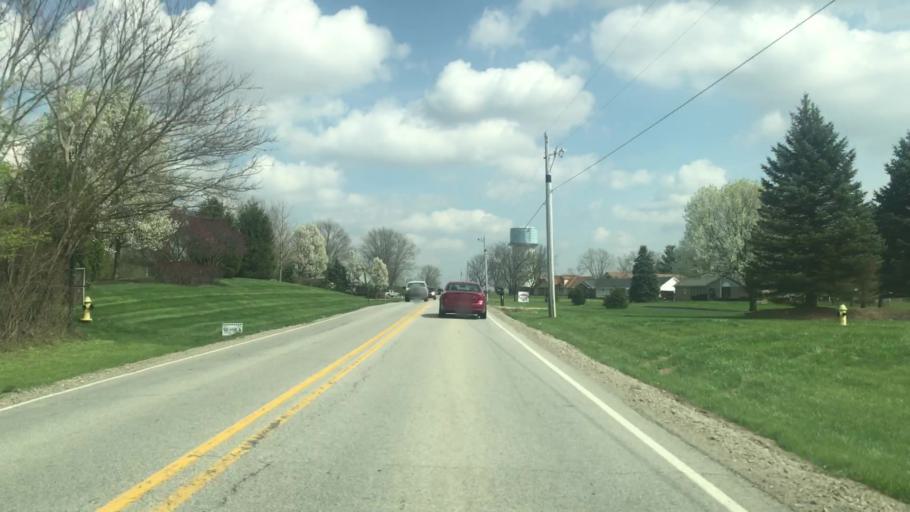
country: US
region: Indiana
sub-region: Johnson County
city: Waterloo
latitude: 39.5504
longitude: -86.2080
